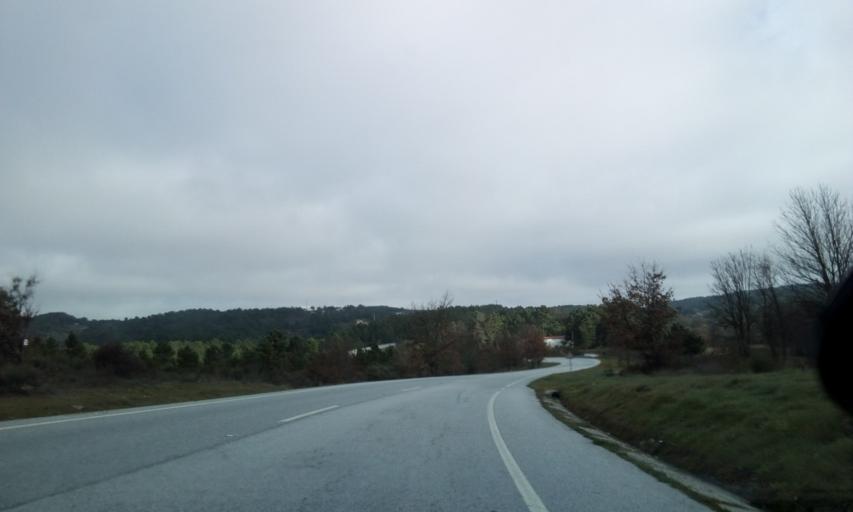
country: PT
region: Guarda
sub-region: Aguiar da Beira
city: Aguiar da Beira
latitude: 40.7748
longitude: -7.5054
